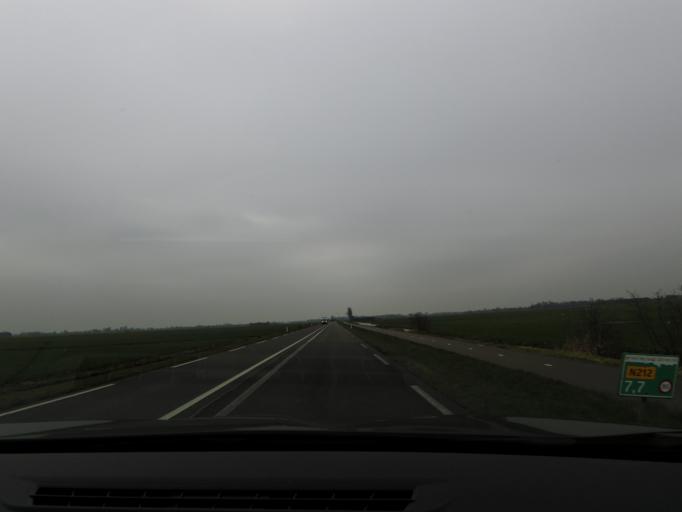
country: NL
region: Utrecht
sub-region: Gemeente Woerden
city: Woerden
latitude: 52.1482
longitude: 4.9114
